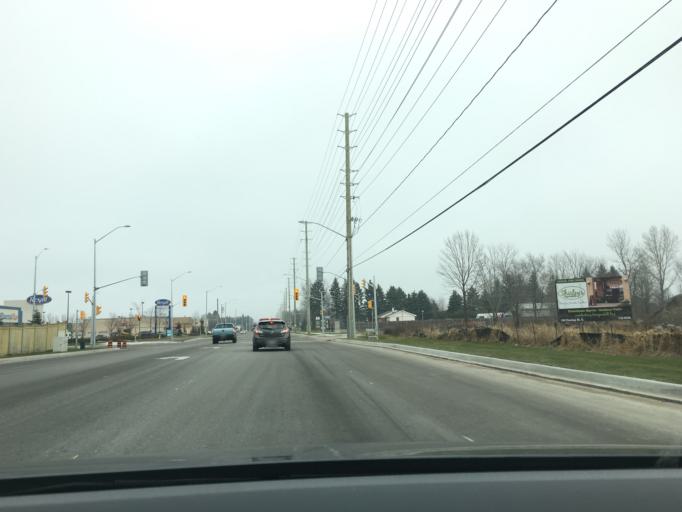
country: CA
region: Ontario
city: Innisfil
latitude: 44.3356
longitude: -79.7108
